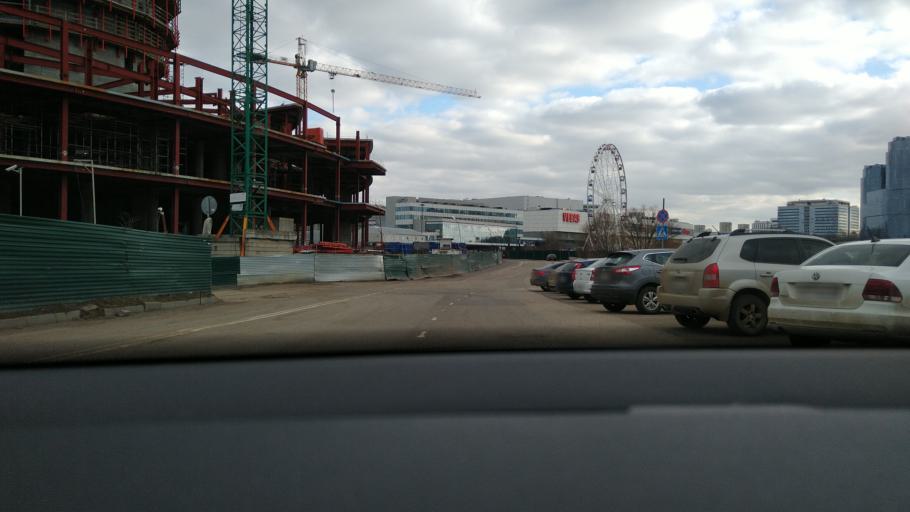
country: RU
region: Moscow
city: Strogino
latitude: 55.8251
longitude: 37.3821
